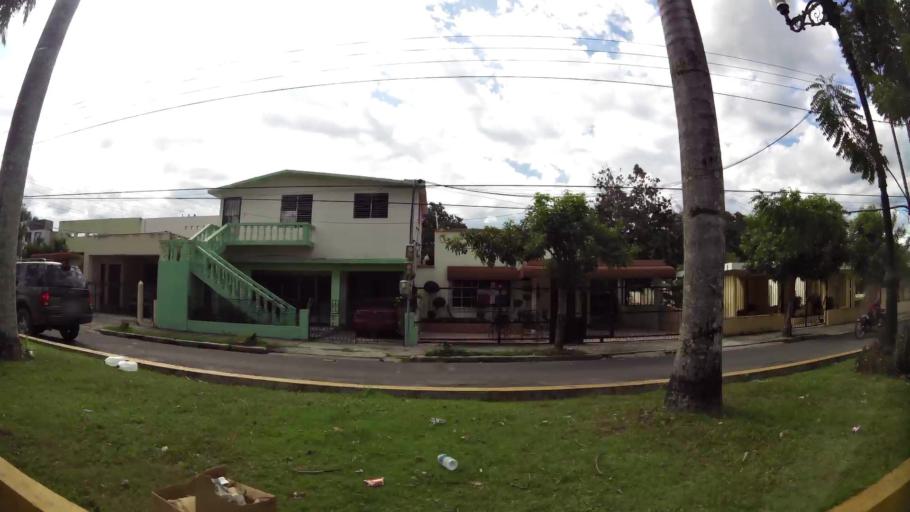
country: DO
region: La Vega
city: Concepcion de La Vega
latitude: 19.2207
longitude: -70.5310
